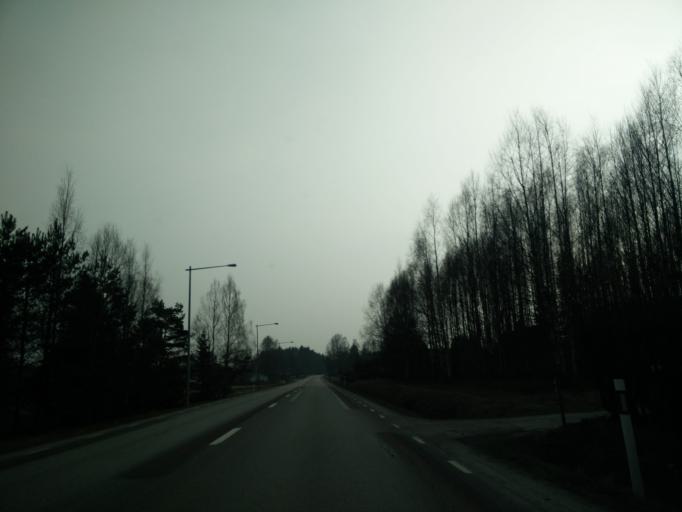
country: SE
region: Vaermland
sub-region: Forshaga Kommun
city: Forshaga
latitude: 59.4949
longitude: 13.4285
